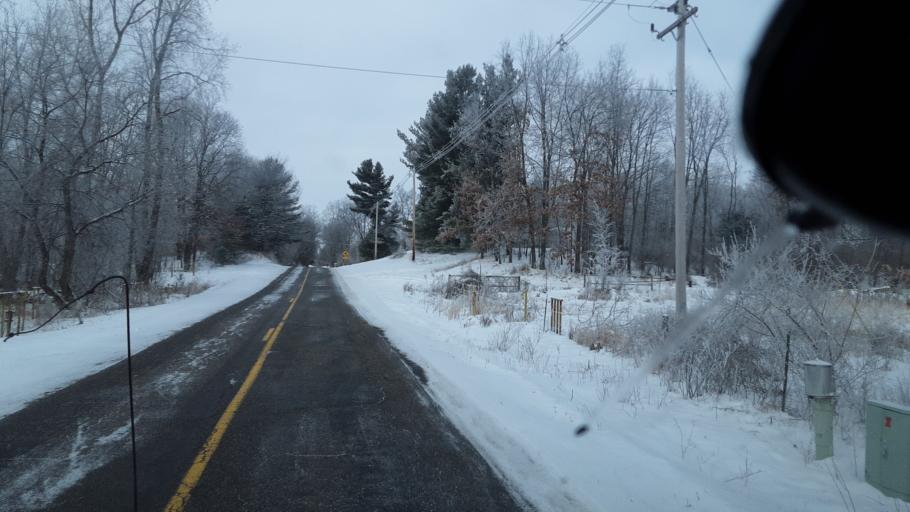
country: US
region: Michigan
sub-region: Ingham County
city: Leslie
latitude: 42.4656
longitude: -84.5478
